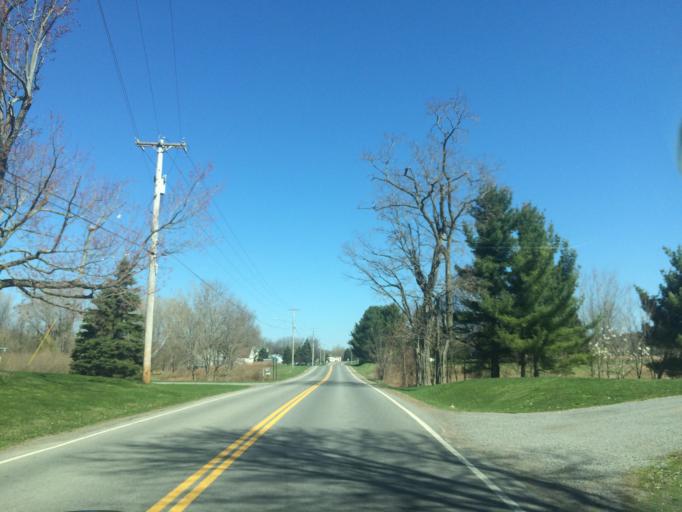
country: US
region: New York
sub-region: Wayne County
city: Palmyra
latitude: 43.0655
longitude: -77.2589
